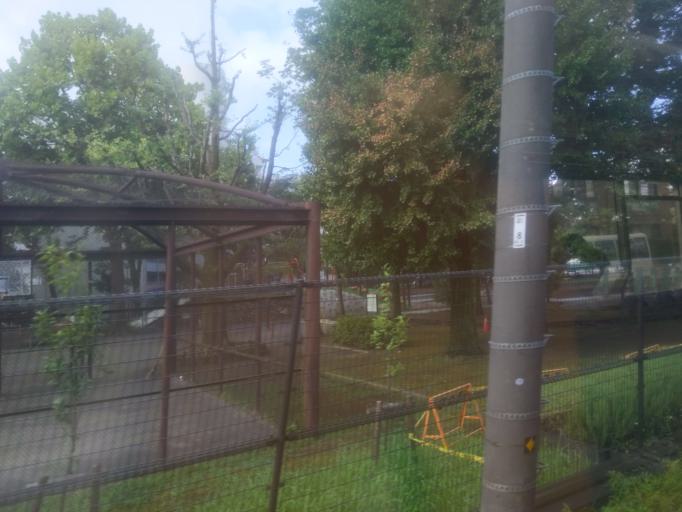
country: JP
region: Tokyo
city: Tokyo
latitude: 35.7151
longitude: 139.6804
